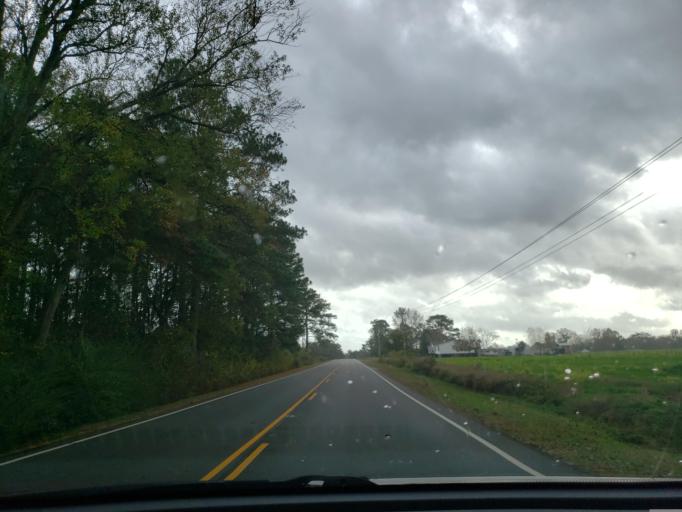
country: US
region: North Carolina
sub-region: Duplin County
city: Beulaville
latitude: 34.8539
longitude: -77.8733
